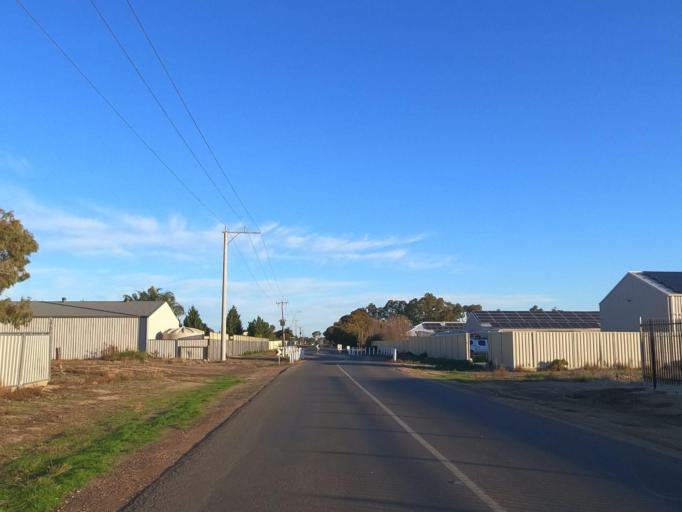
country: AU
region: Victoria
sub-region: Swan Hill
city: Swan Hill
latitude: -35.3287
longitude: 143.5348
